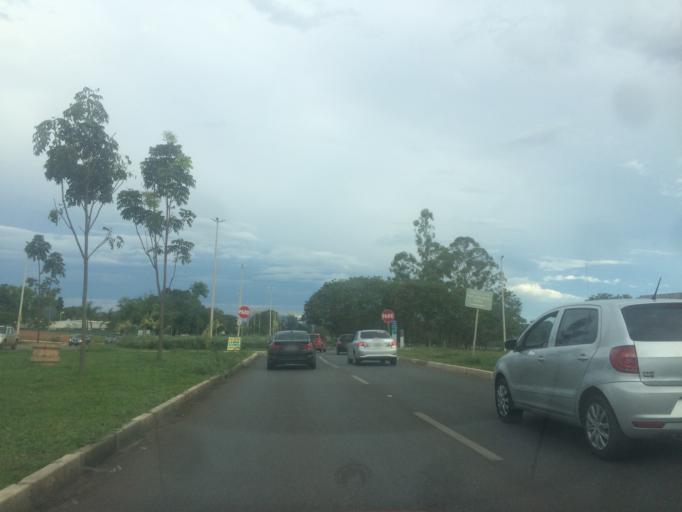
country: BR
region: Federal District
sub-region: Brasilia
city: Brasilia
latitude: -15.8050
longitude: -47.8686
